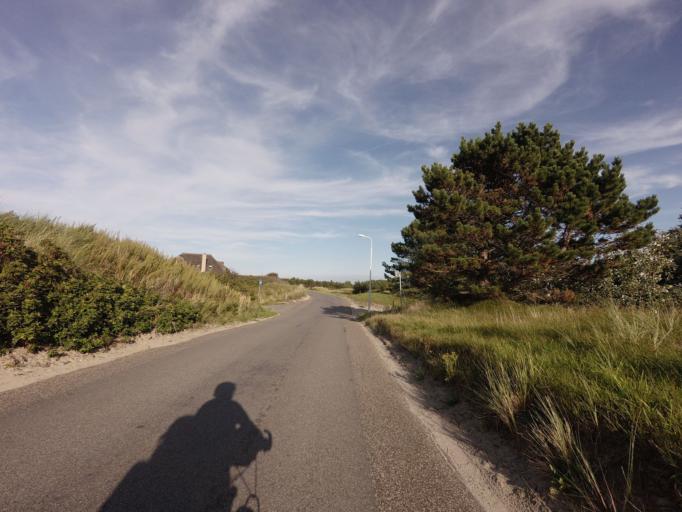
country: NL
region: Friesland
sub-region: Gemeente Ameland
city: Nes
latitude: 53.4555
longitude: 5.7937
